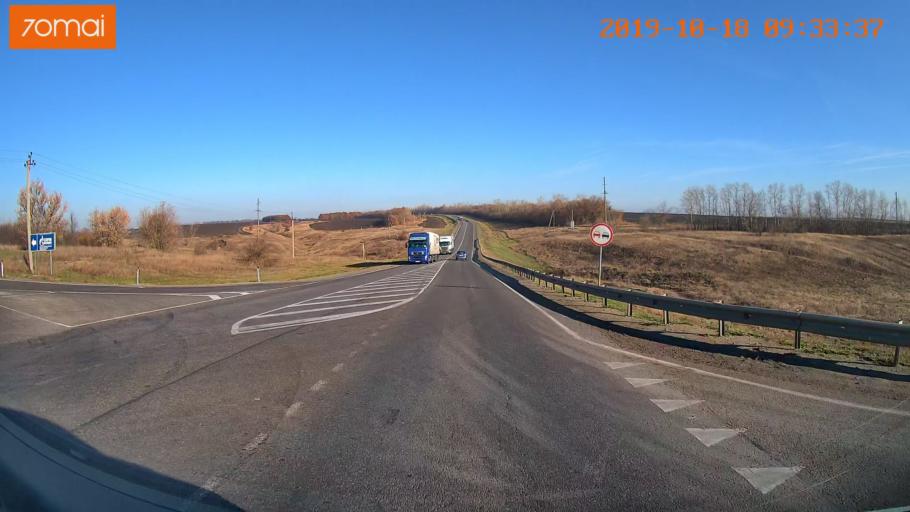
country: RU
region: Tula
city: Yefremov
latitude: 53.1691
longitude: 38.1515
